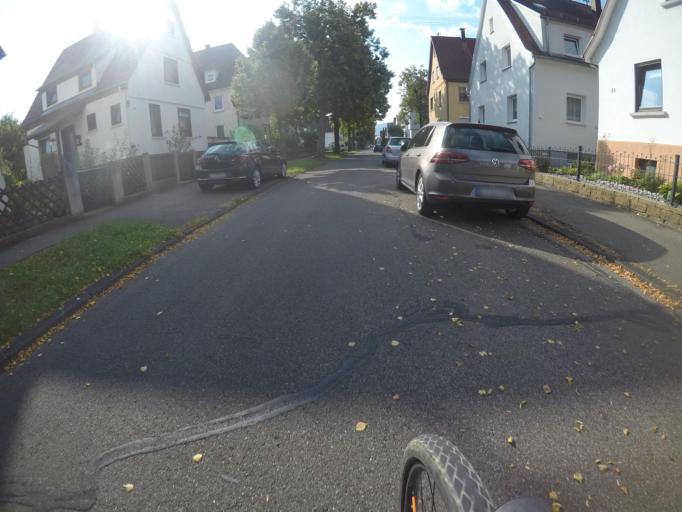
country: DE
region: Baden-Wuerttemberg
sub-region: Tuebingen Region
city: Metzingen
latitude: 48.5431
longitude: 9.2815
